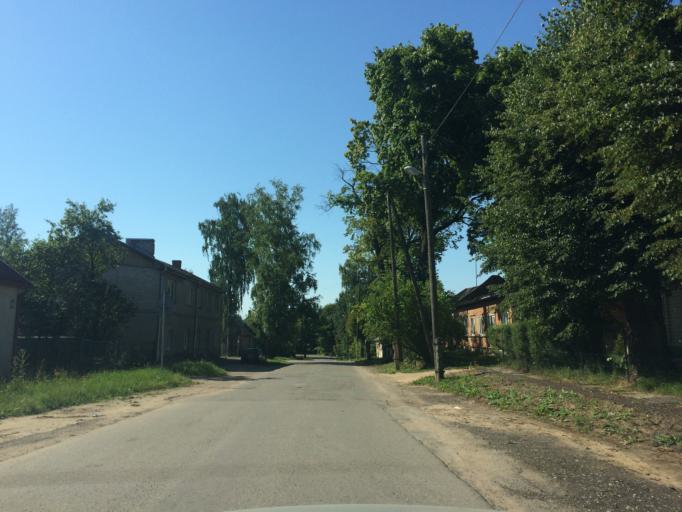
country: LV
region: Rezekne
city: Rezekne
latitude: 56.5071
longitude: 27.3279
